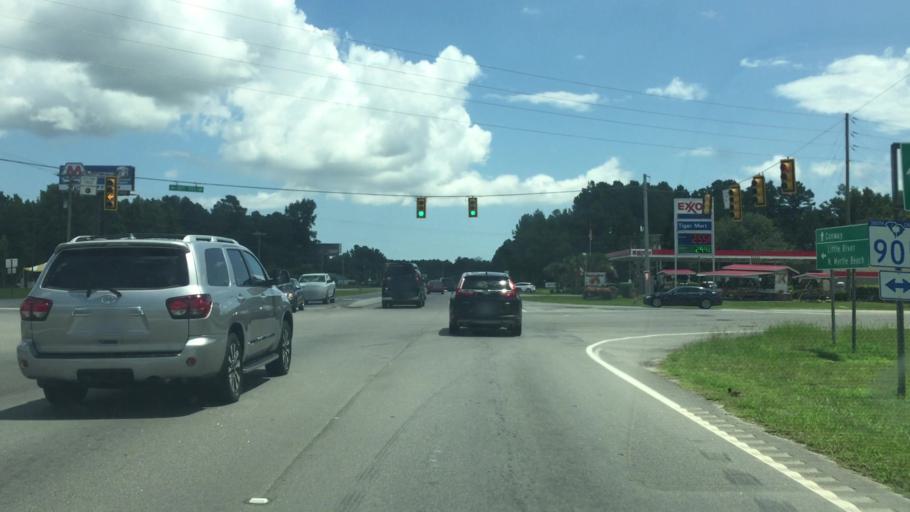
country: US
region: South Carolina
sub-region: Horry County
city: North Myrtle Beach
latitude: 33.9389
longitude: -78.7336
